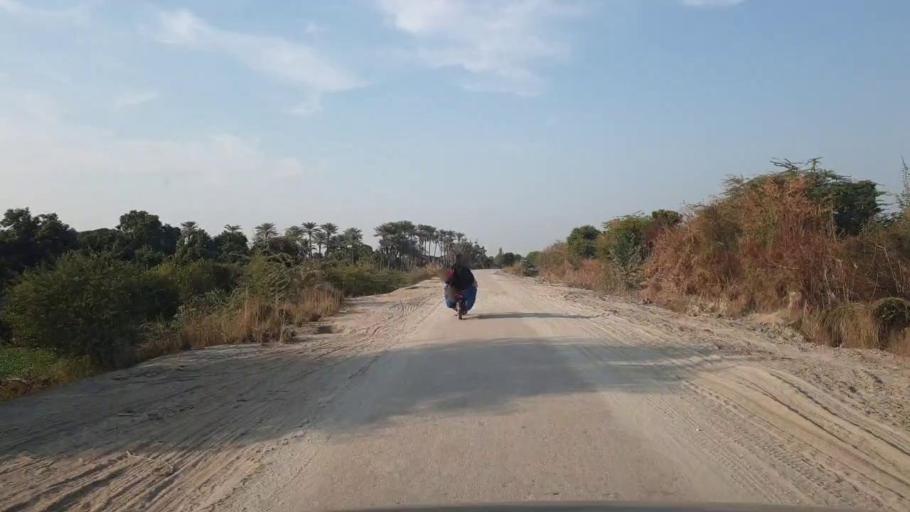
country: PK
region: Sindh
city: Shahpur Chakar
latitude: 26.1536
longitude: 68.6414
